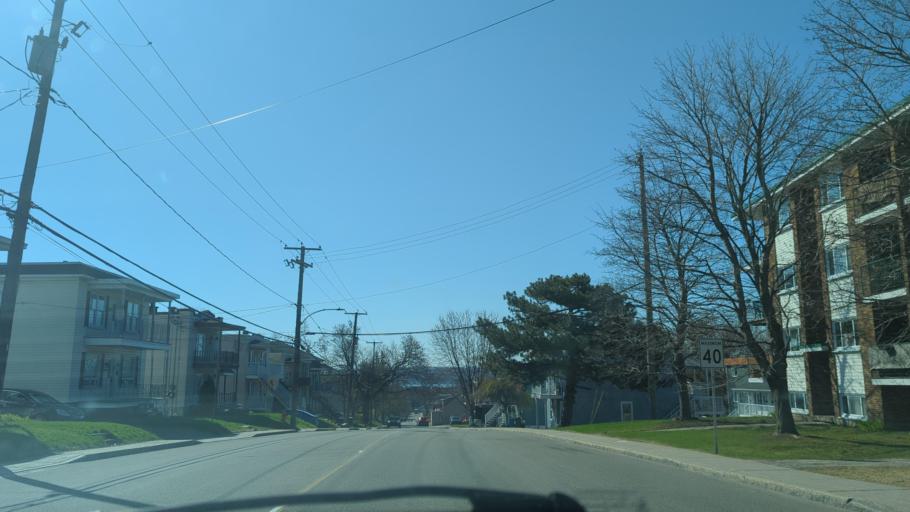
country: CA
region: Quebec
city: Quebec
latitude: 46.8549
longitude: -71.2157
